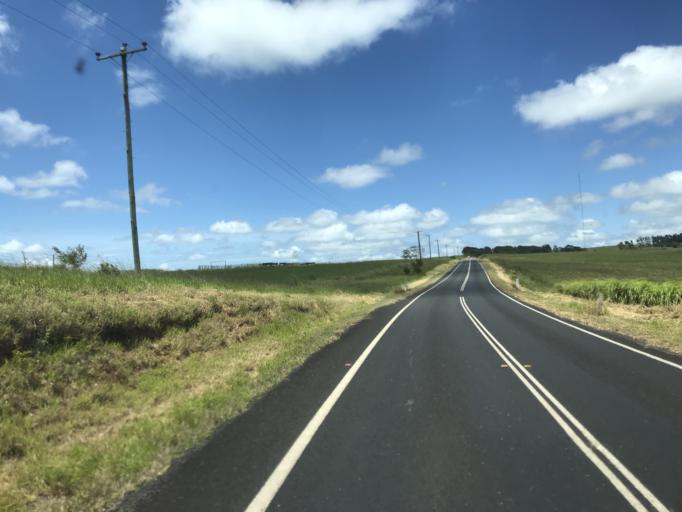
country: AU
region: Queensland
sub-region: Tablelands
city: Ravenshoe
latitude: -17.4902
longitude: 145.4736
